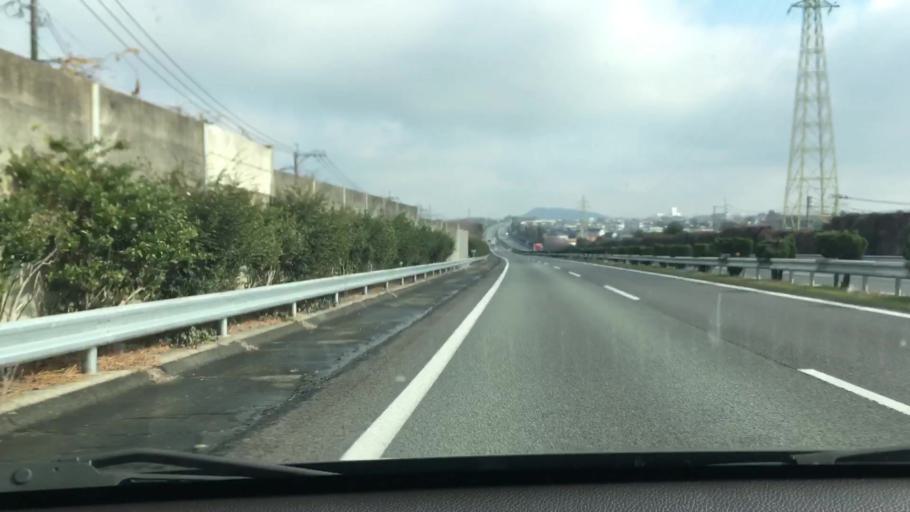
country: JP
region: Kumamoto
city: Ueki
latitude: 32.8601
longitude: 130.7459
